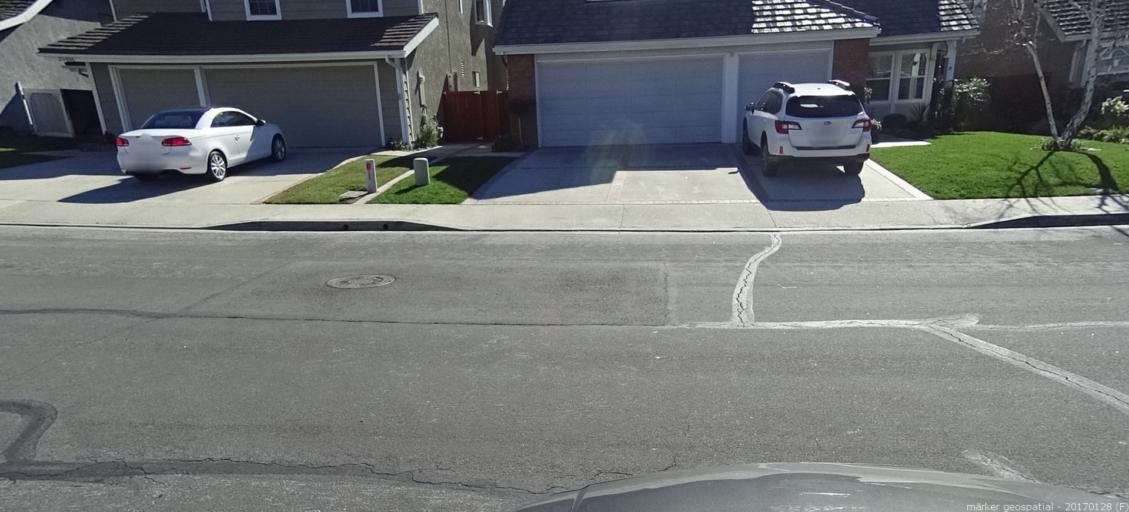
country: US
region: California
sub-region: Orange County
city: Lake Forest
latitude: 33.6516
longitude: -117.6866
